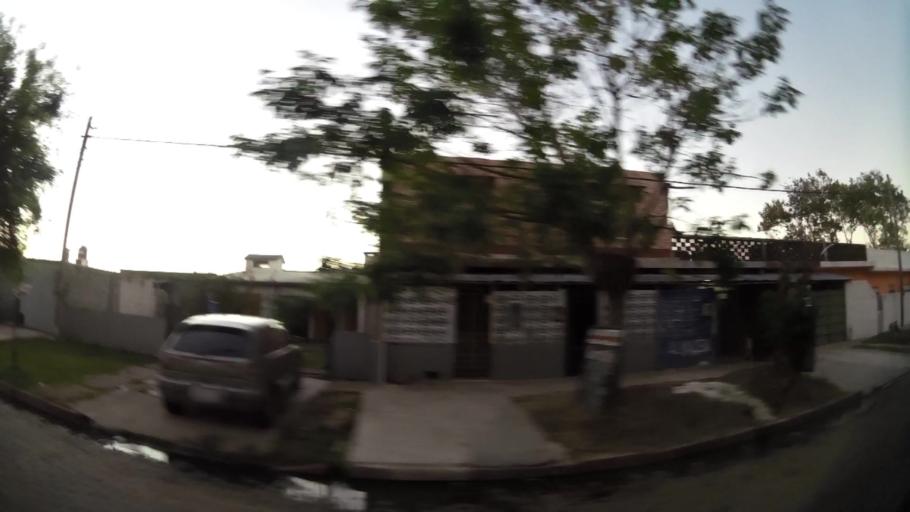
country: UY
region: Canelones
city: Toledo
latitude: -34.8141
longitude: -56.1400
